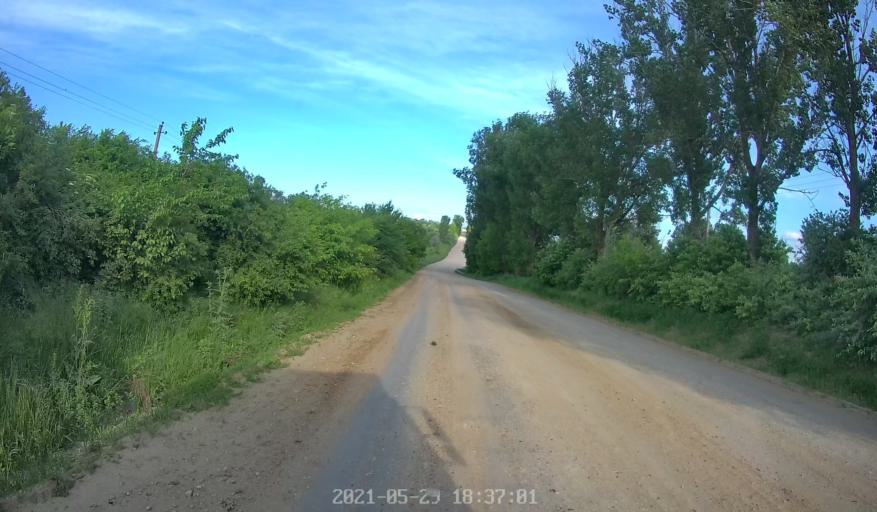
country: MD
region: Chisinau
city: Singera
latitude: 46.8050
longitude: 28.9280
